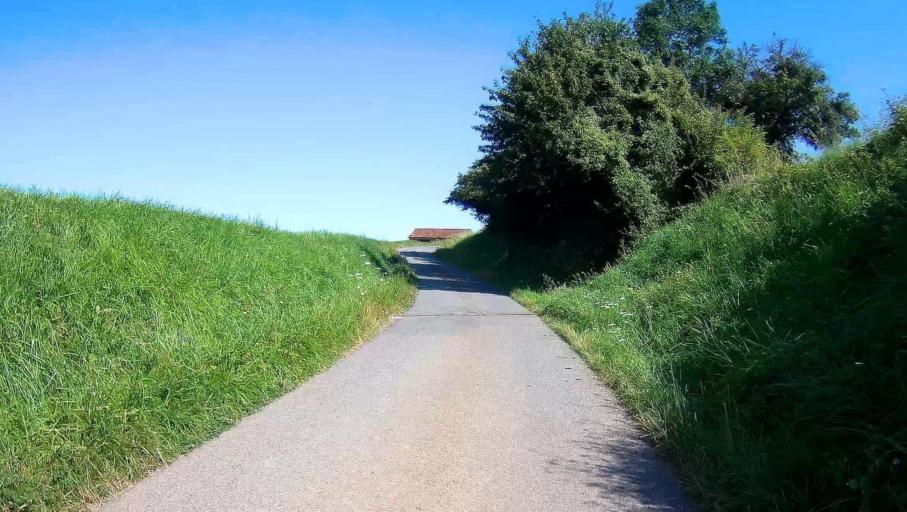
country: FR
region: Bourgogne
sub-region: Departement de Saone-et-Loire
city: Couches
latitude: 46.8485
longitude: 4.5686
